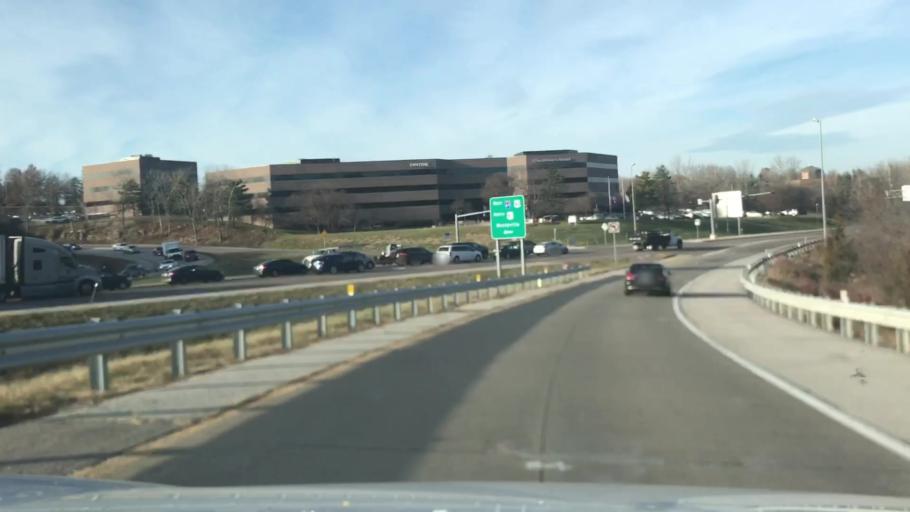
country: US
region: Missouri
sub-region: Saint Louis County
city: Manchester
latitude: 38.6434
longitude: -90.5093
